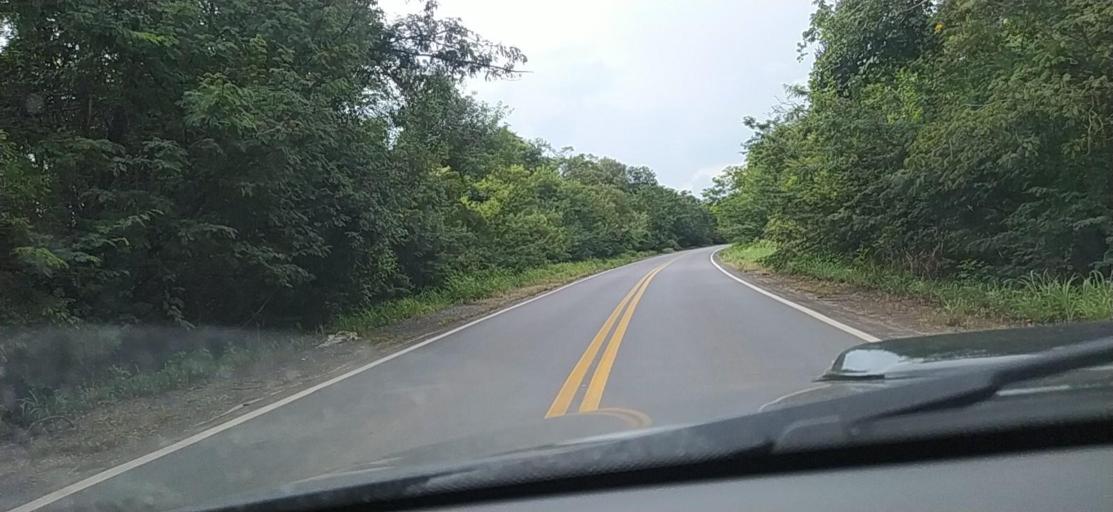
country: BR
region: Minas Gerais
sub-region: Francisco Sa
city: Francisco Sa
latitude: -16.5259
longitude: -43.6801
